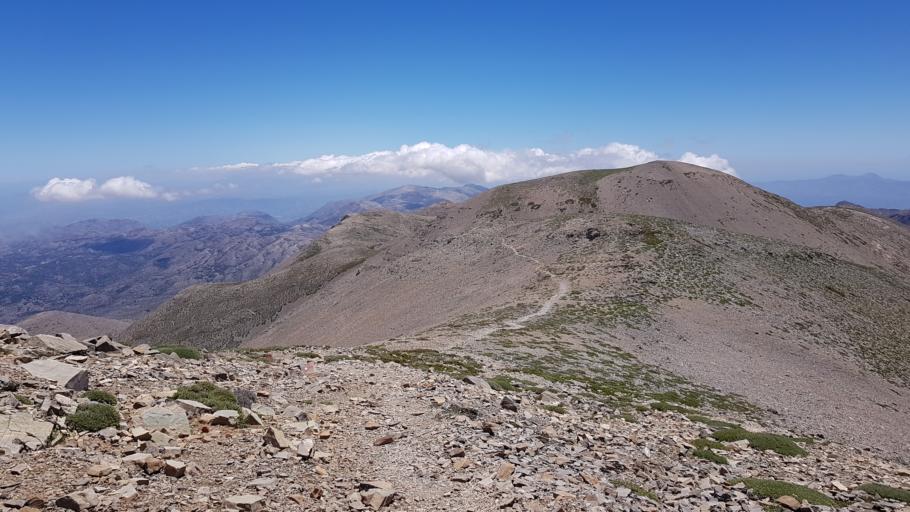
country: GR
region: Crete
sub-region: Nomos Rethymnis
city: Zoniana
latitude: 35.2259
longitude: 24.7719
